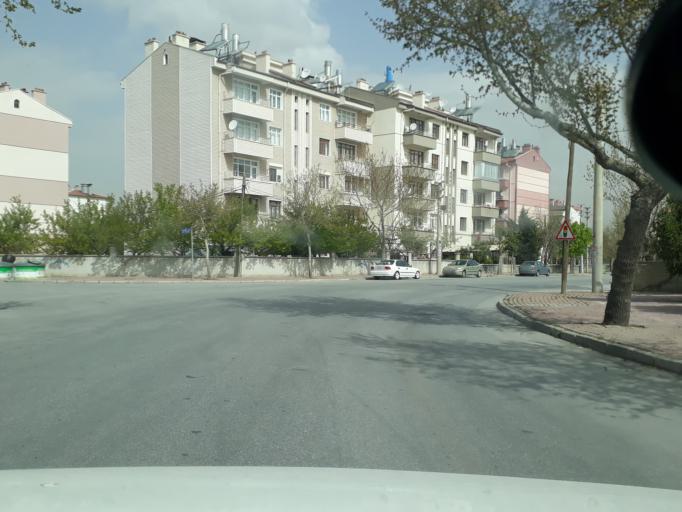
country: TR
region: Konya
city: Selcuklu
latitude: 37.9357
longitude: 32.4993
